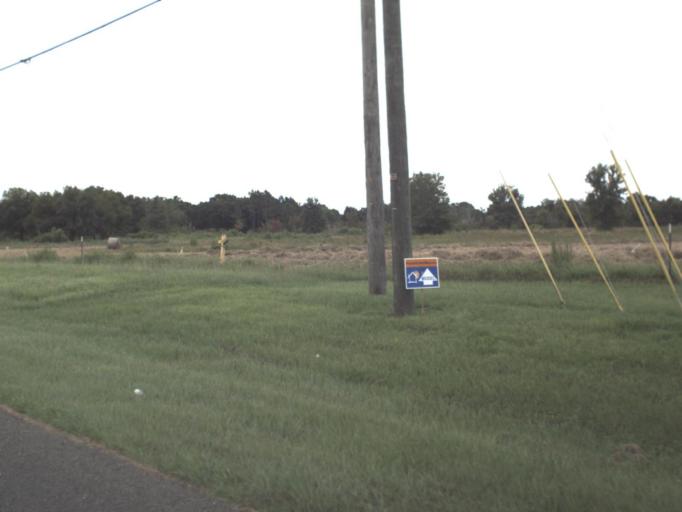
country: US
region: Florida
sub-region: Pasco County
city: Wesley Chapel
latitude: 28.2312
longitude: -82.2955
